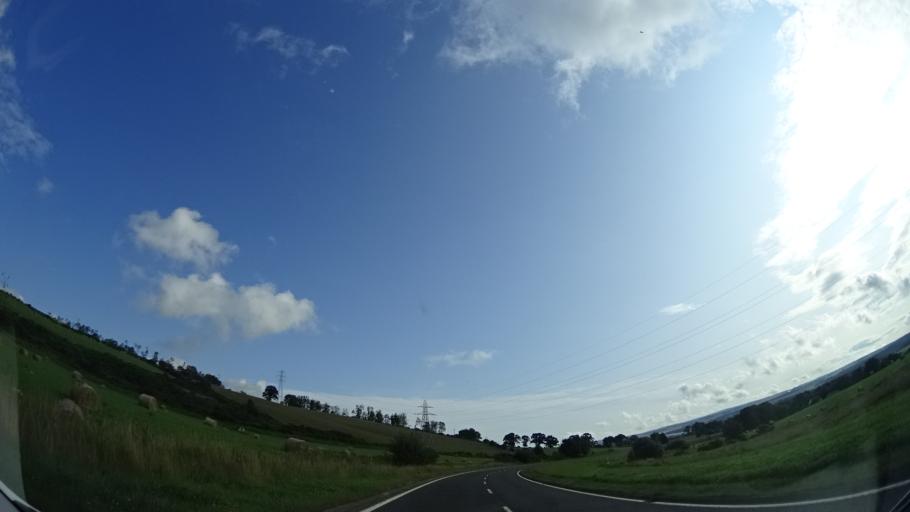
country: GB
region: Scotland
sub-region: Highland
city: Conon Bridge
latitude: 57.5782
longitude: -4.4460
